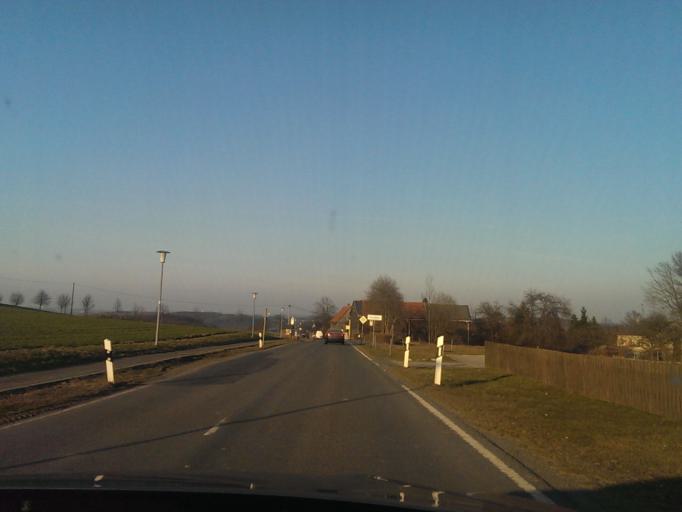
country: DE
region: Saxony
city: Weischlitz
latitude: 50.4058
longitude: 12.0428
